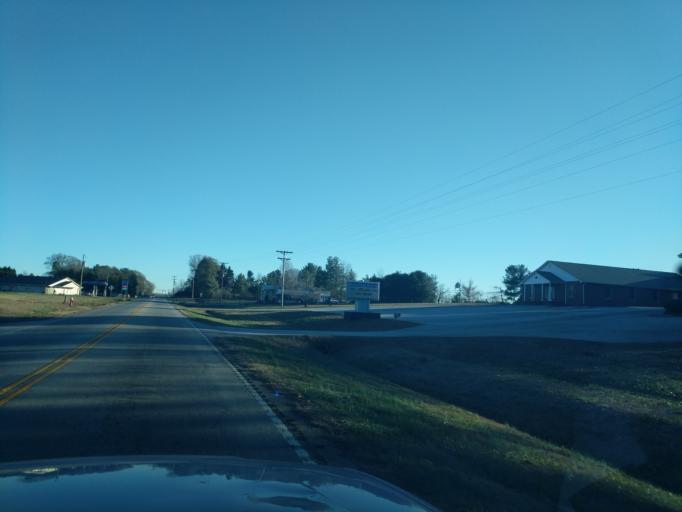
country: US
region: South Carolina
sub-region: Oconee County
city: Westminster
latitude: 34.6287
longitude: -83.0574
